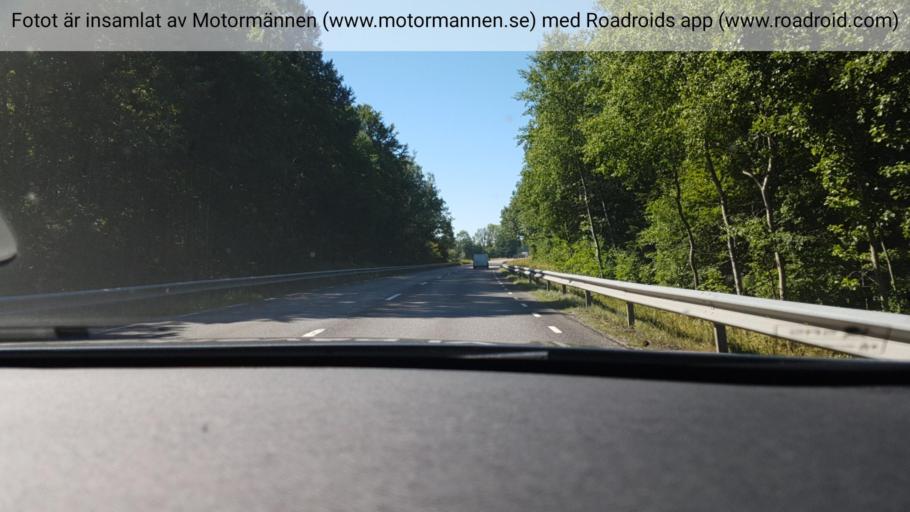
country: SE
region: Joenkoeping
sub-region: Habo Kommun
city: Habo
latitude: 57.9570
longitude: 14.1065
